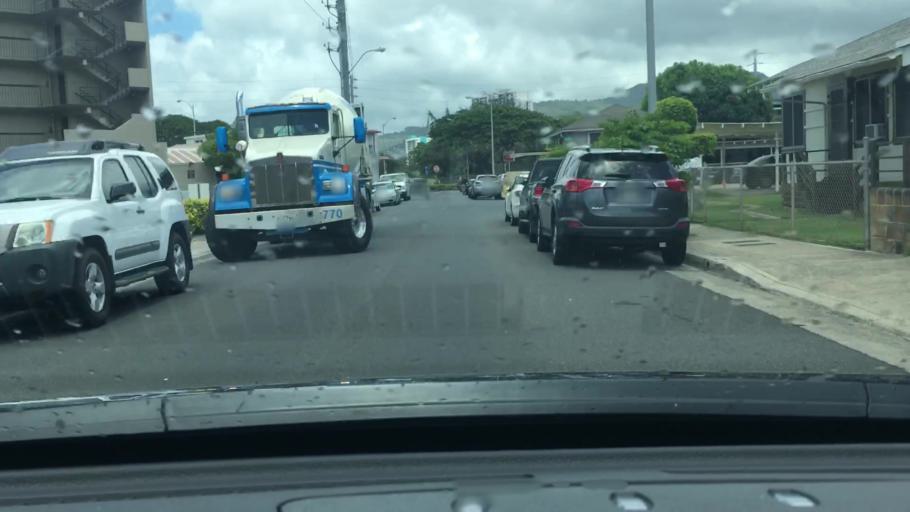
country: US
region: Hawaii
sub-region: Honolulu County
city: Honolulu
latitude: 21.2751
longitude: -157.8146
